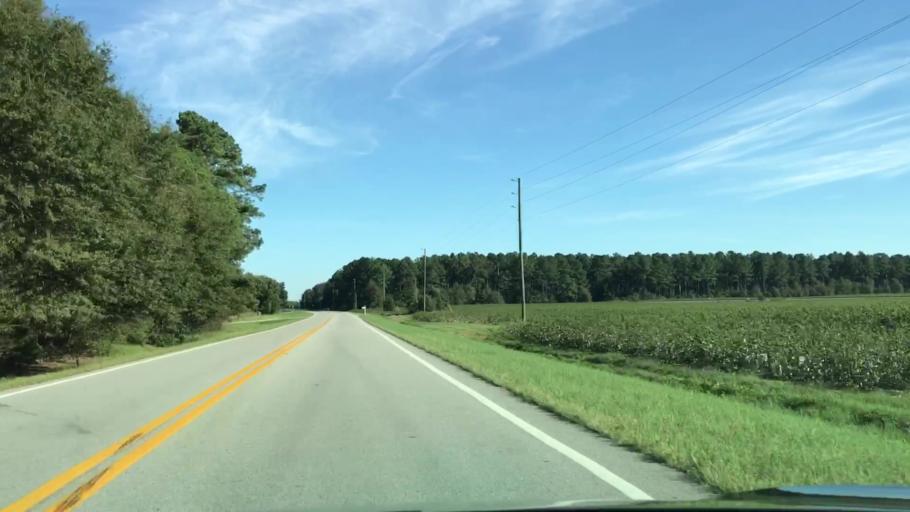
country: US
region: Georgia
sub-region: Glascock County
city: Gibson
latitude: 33.3126
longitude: -82.5405
